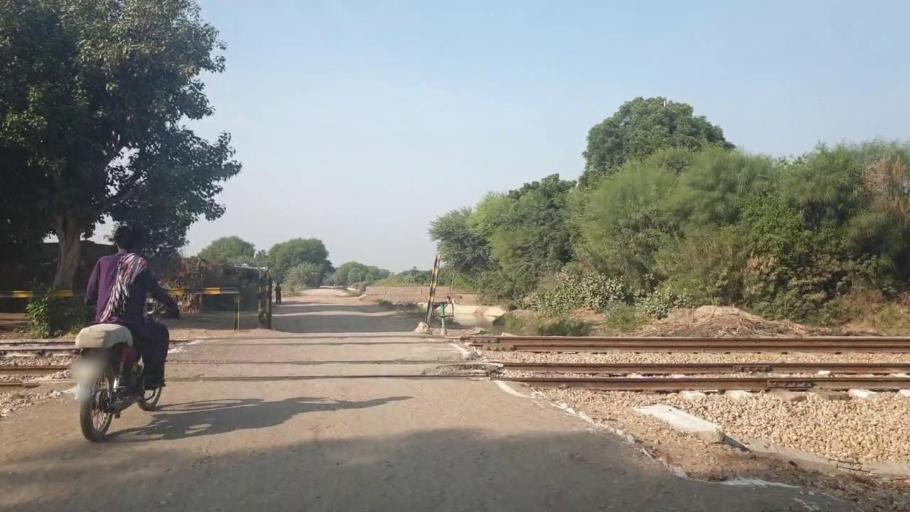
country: PK
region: Sindh
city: Tando Jam
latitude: 25.4124
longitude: 68.4654
